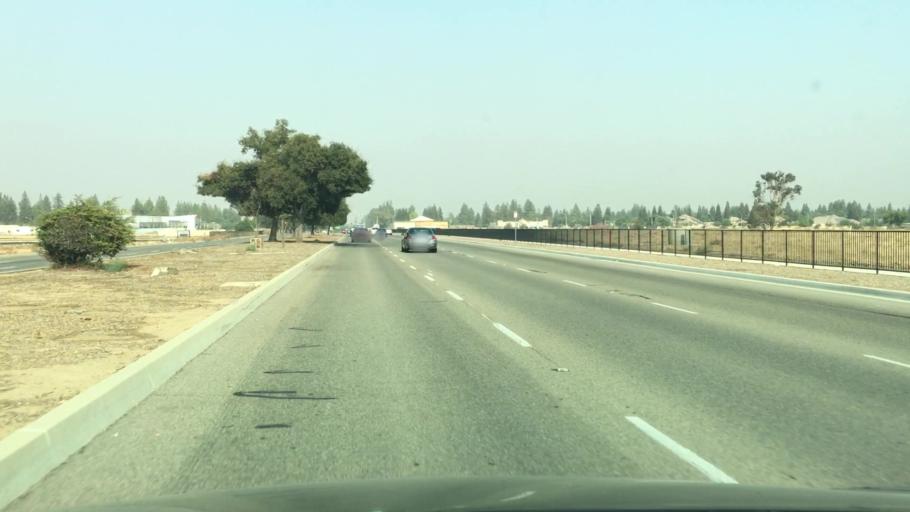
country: US
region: California
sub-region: Fresno County
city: West Park
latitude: 36.8370
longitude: -119.8684
